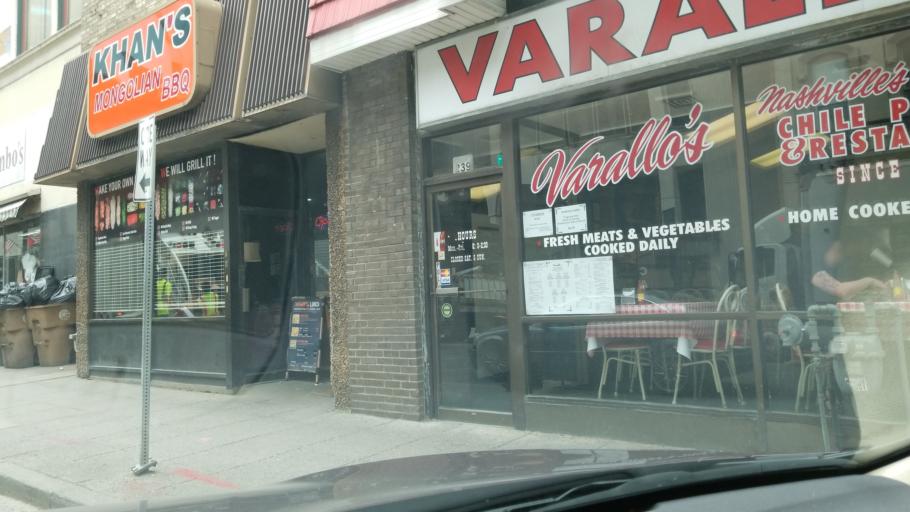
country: US
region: Tennessee
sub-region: Davidson County
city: Nashville
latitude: 36.1648
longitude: -86.7796
